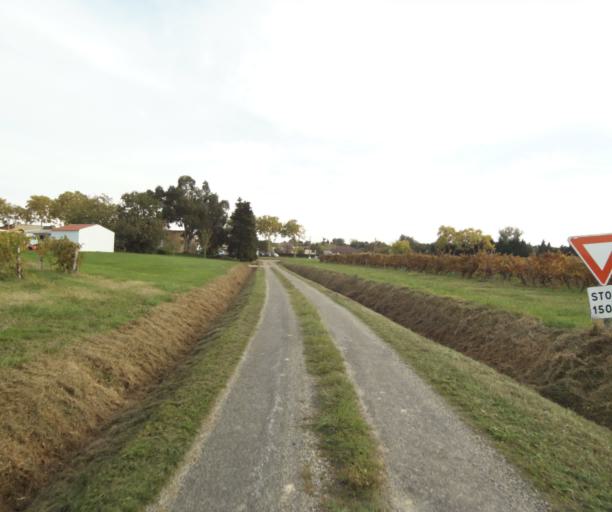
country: FR
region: Midi-Pyrenees
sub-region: Departement du Tarn-et-Garonne
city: Campsas
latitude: 43.9000
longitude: 1.3212
